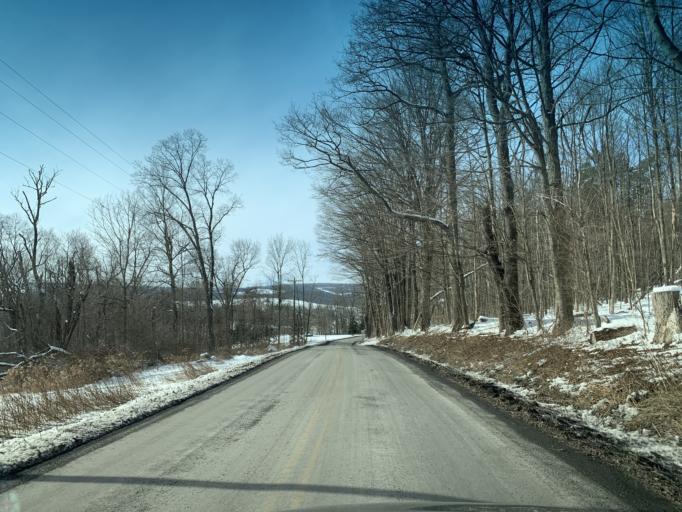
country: US
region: Maryland
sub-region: Allegany County
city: Frostburg
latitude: 39.6210
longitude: -78.9347
